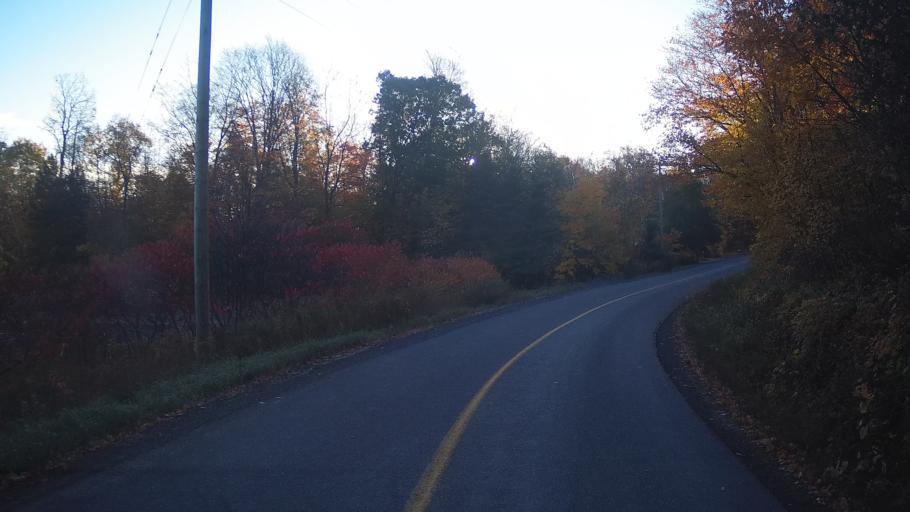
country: CA
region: Ontario
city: Arnprior
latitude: 45.3470
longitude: -76.3384
